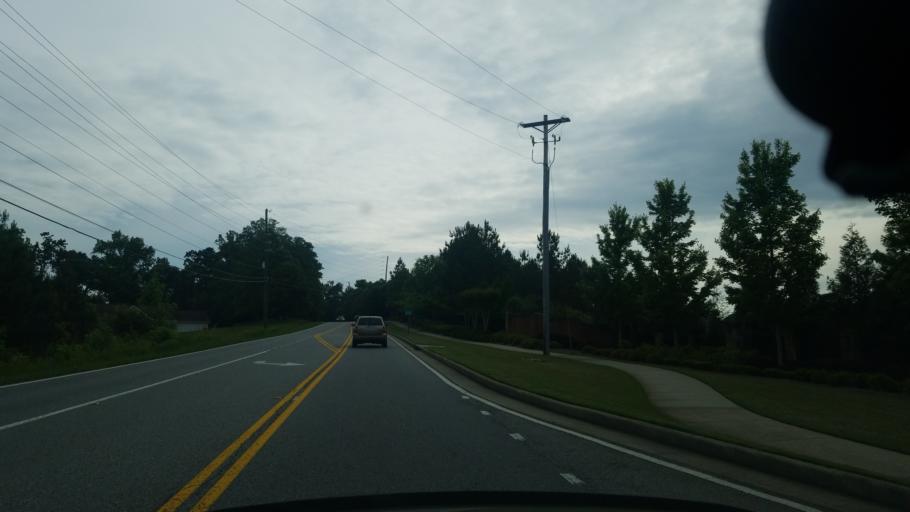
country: US
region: Georgia
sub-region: Gwinnett County
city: Suwanee
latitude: 34.1086
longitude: -84.1282
